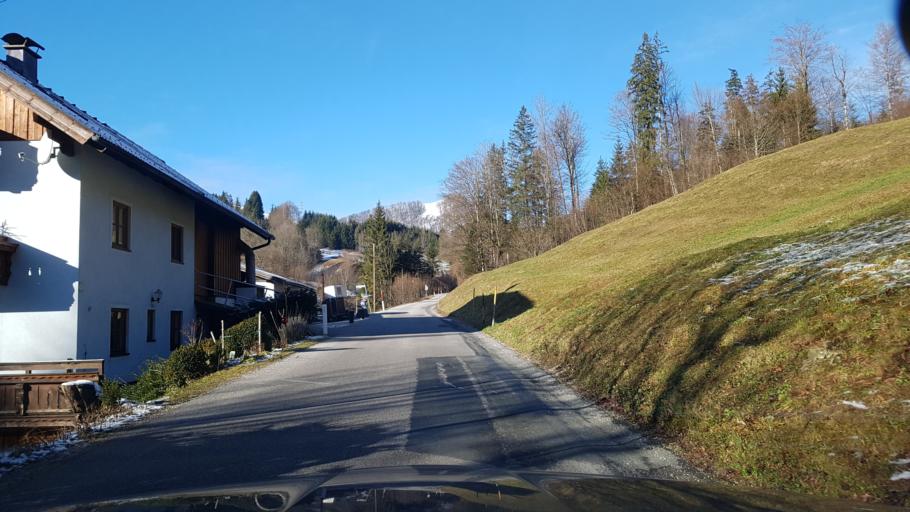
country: AT
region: Salzburg
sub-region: Politischer Bezirk Salzburg-Umgebung
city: Ebenau
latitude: 47.7682
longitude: 13.1744
